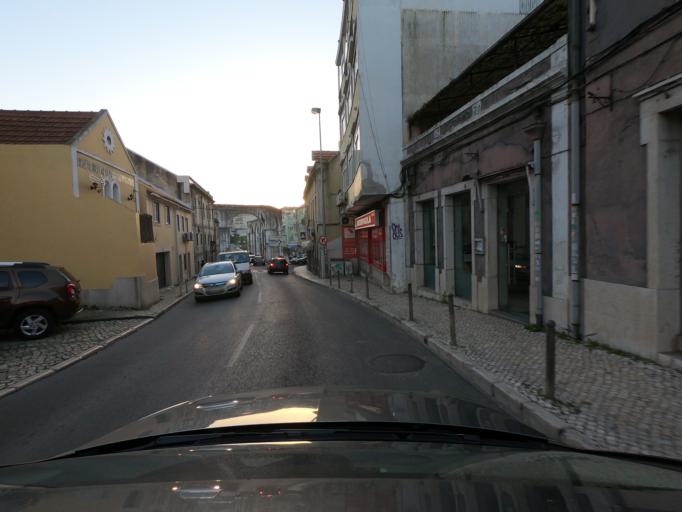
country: PT
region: Lisbon
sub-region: Sintra
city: Queluz
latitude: 38.7574
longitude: -9.2577
